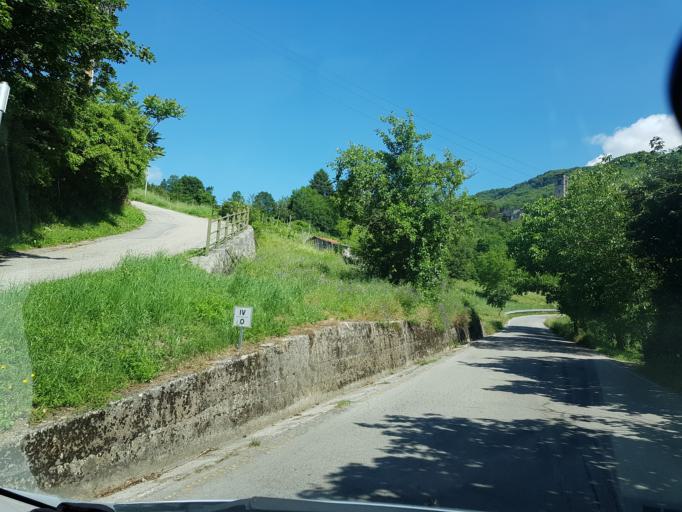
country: IT
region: Tuscany
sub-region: Provincia di Lucca
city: San Romano in Garfagnana
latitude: 44.1662
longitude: 10.3471
